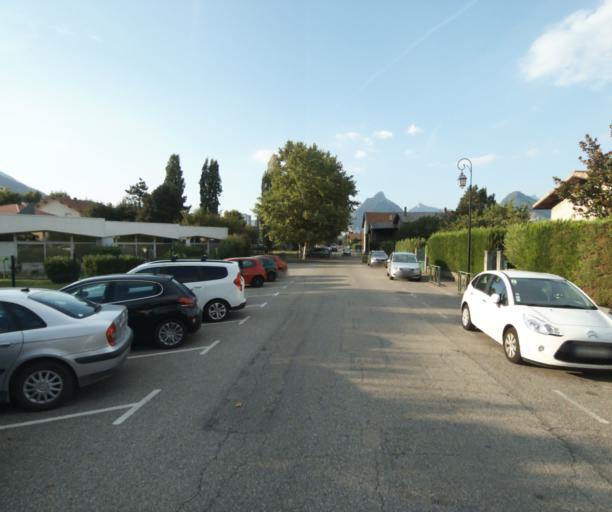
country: FR
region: Rhone-Alpes
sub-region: Departement de l'Isere
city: Seyssinet-Pariset
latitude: 45.1662
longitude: 5.6967
